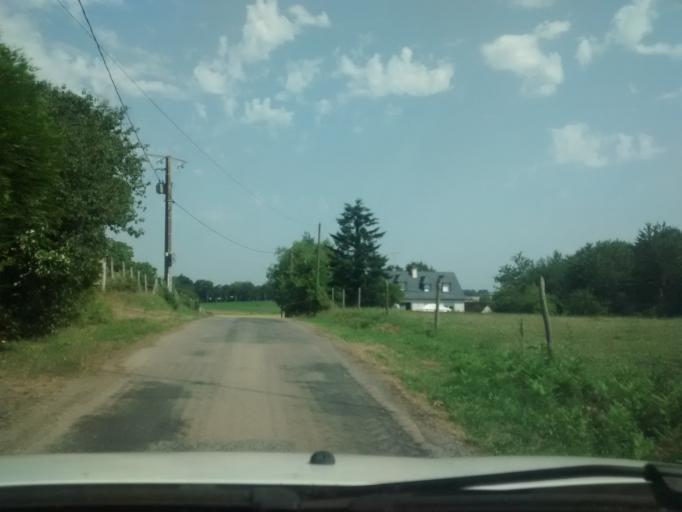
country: FR
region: Brittany
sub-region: Departement d'Ille-et-Vilaine
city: Cesson-Sevigne
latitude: 48.1405
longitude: -1.5946
